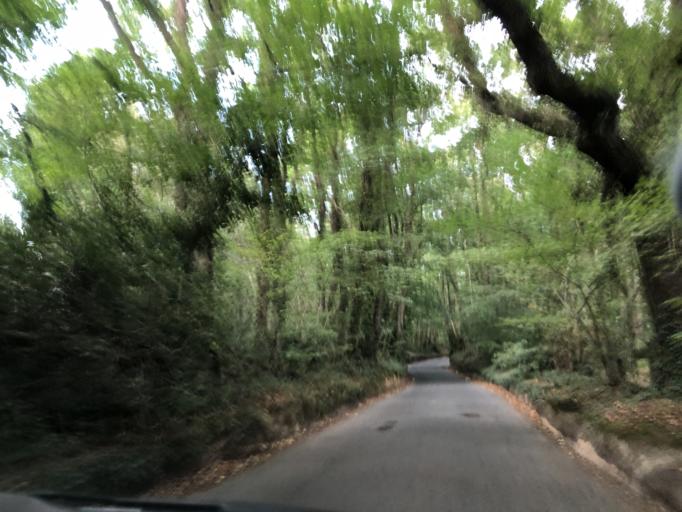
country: GB
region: England
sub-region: East Sussex
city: Bexhill-on-Sea
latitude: 50.8601
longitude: 0.4371
